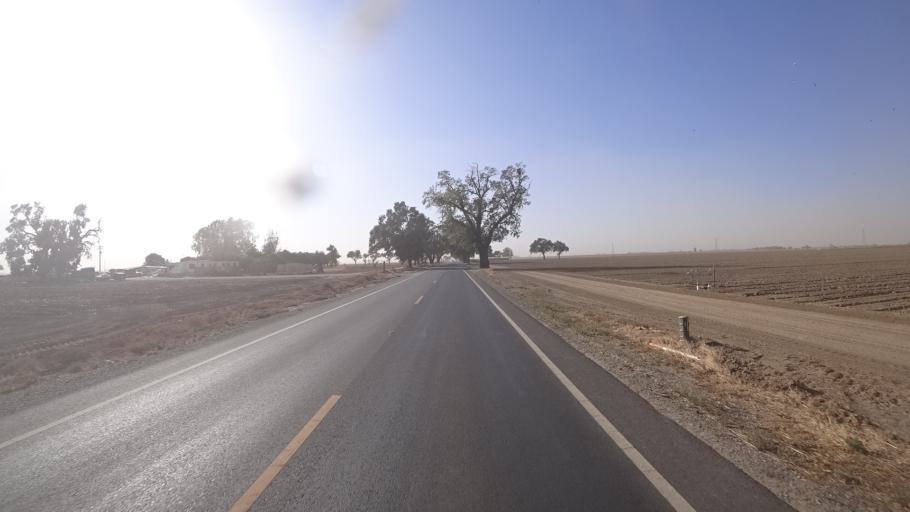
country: US
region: California
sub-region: Yolo County
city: Woodland
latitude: 38.7930
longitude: -121.7615
